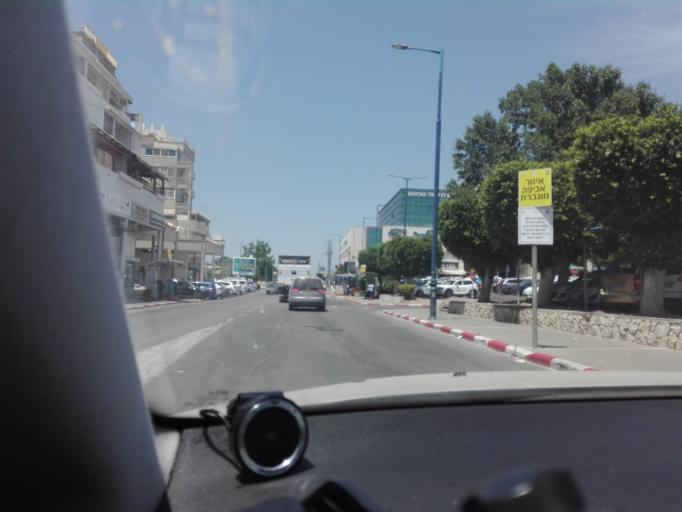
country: IL
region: Central District
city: Bene 'Ayish
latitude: 31.7294
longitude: 34.7464
